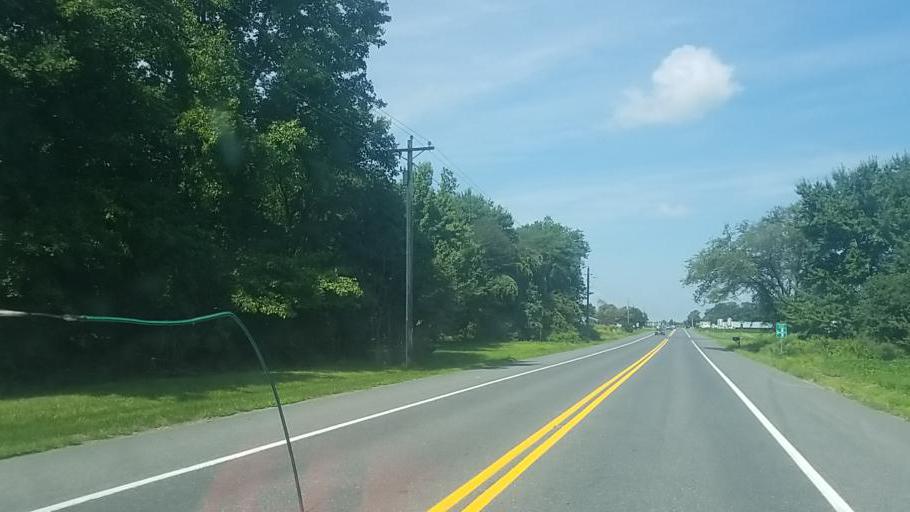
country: US
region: Delaware
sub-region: Sussex County
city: Bridgeville
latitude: 38.8243
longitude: -75.6442
